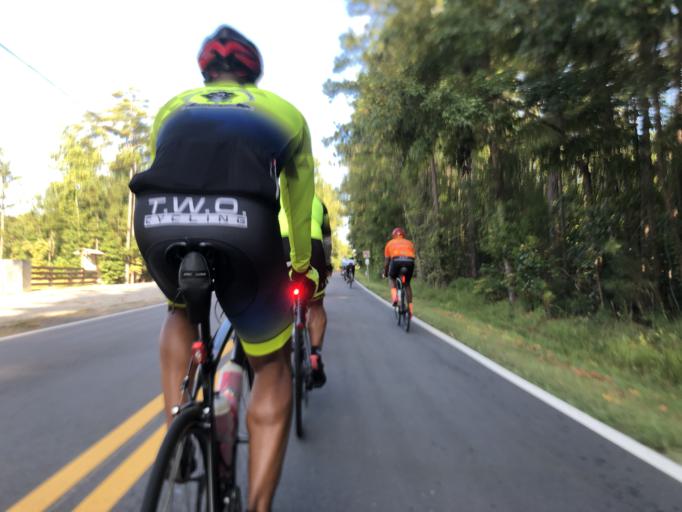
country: US
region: Georgia
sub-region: Fulton County
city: Chattahoochee Hills
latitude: 33.5823
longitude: -84.7014
